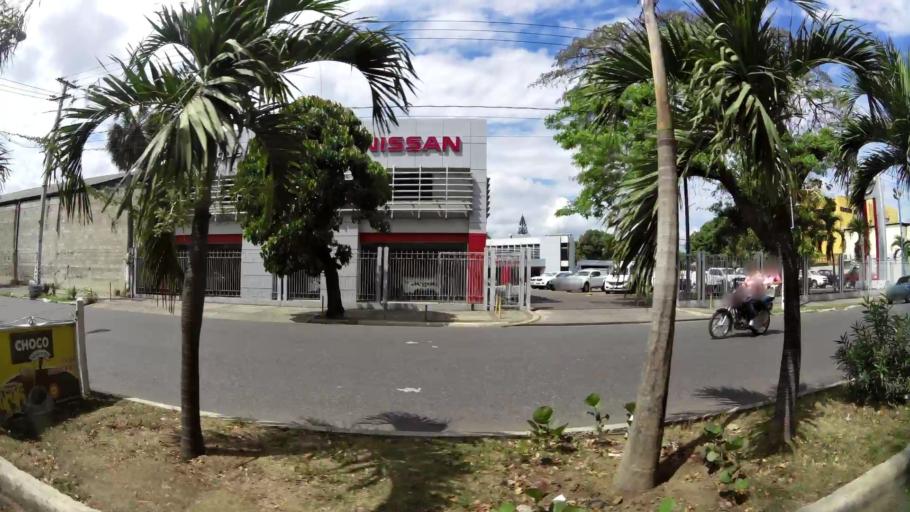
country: DO
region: Santiago
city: Santiago de los Caballeros
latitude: 19.4616
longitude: -70.7101
